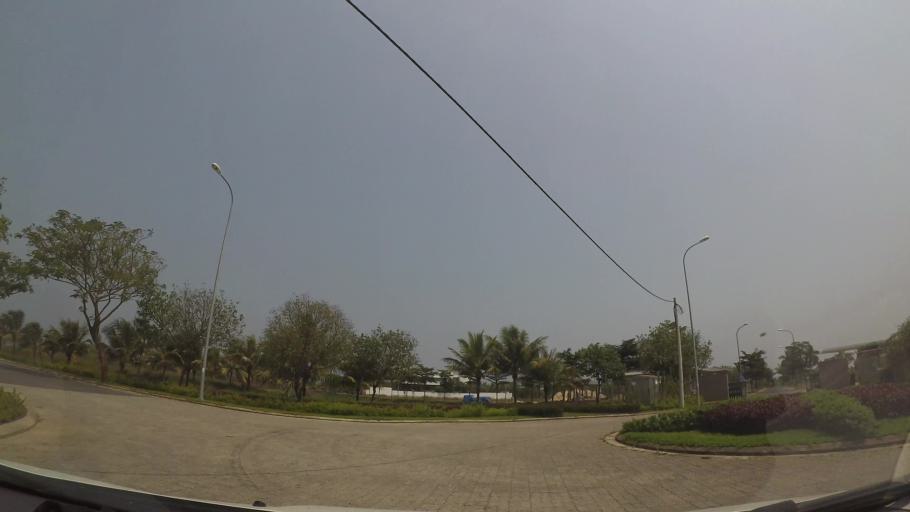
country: VN
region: Da Nang
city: Ngu Hanh Son
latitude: 15.9703
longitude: 108.2644
